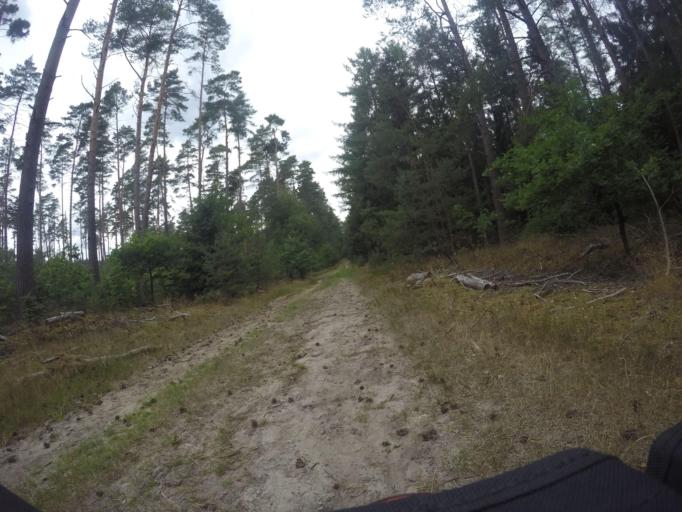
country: DE
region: Lower Saxony
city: Thomasburg
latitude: 53.2333
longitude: 10.6942
